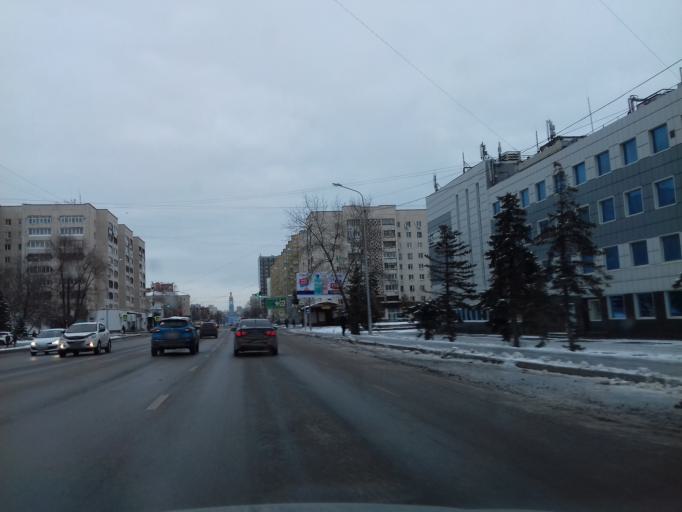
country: RU
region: Bashkortostan
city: Ufa
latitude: 54.7292
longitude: 55.9612
